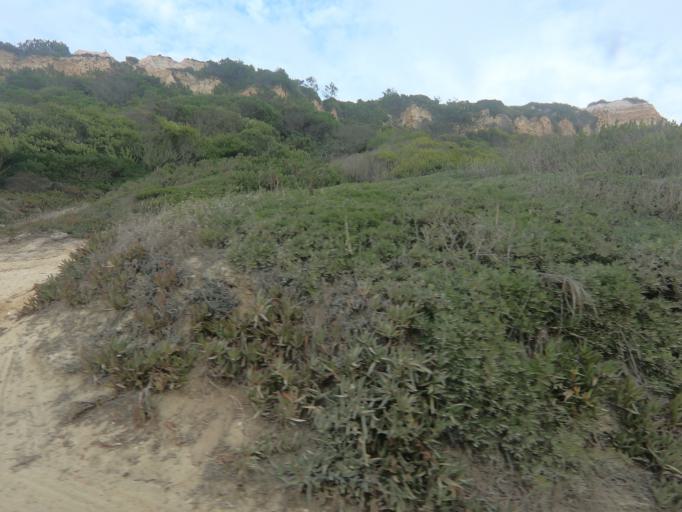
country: PT
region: Setubal
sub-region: Almada
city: Charneca
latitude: 38.5599
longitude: -9.1901
